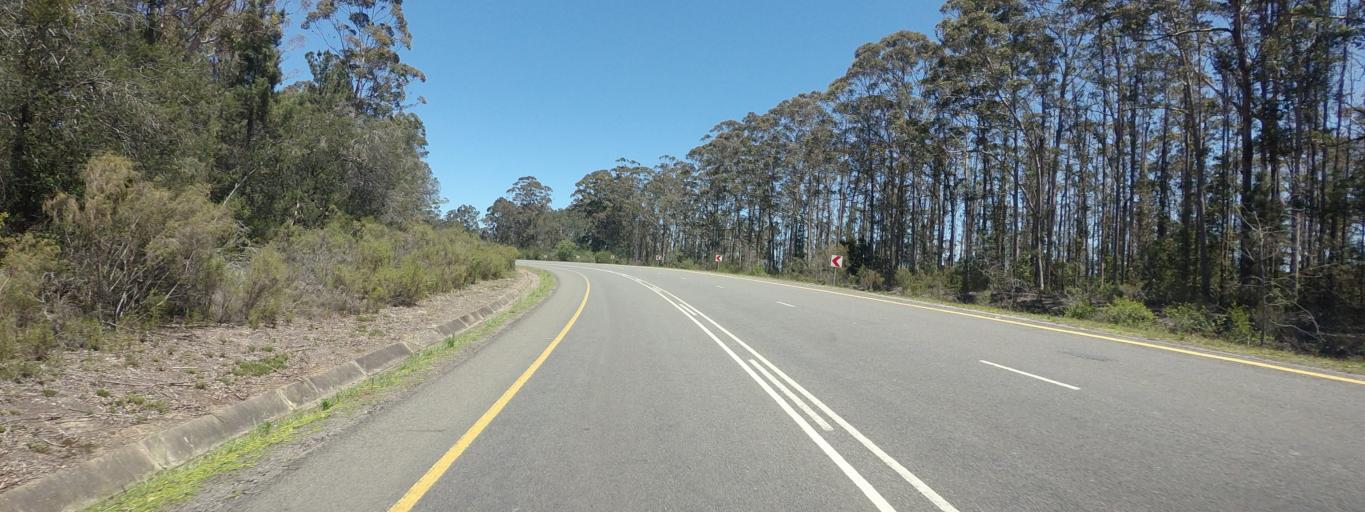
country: ZA
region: Western Cape
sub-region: Eden District Municipality
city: Plettenberg Bay
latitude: -33.9703
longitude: 23.4334
